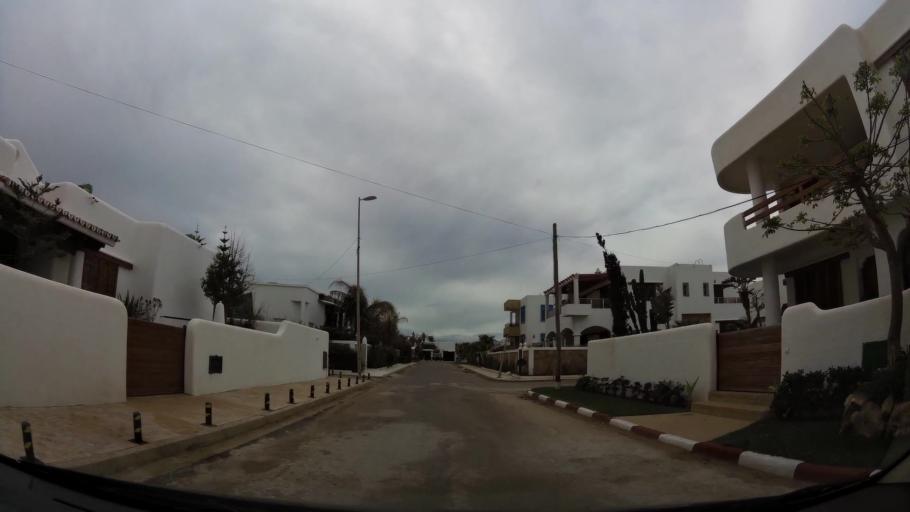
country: MA
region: Tanger-Tetouan
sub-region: Tetouan
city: Martil
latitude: 35.7427
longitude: -5.3419
